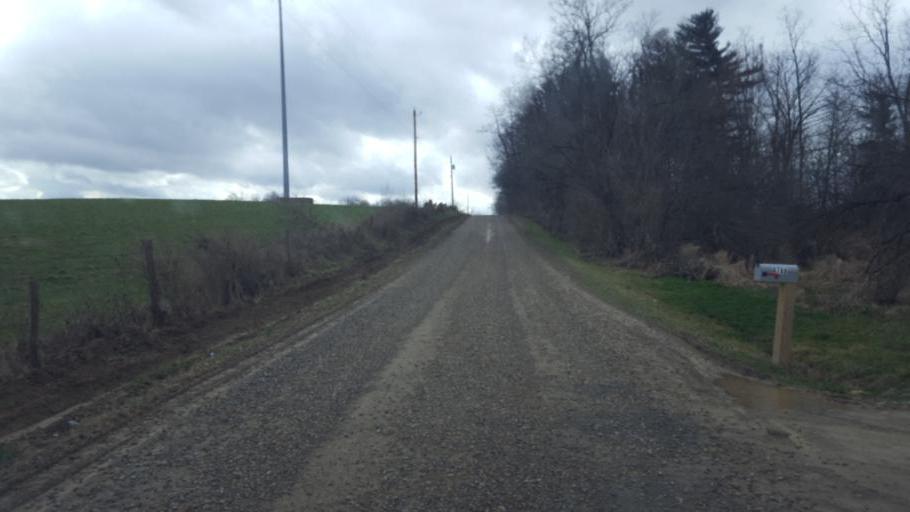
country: US
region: Ohio
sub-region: Knox County
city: Centerburg
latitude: 40.3399
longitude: -82.6086
